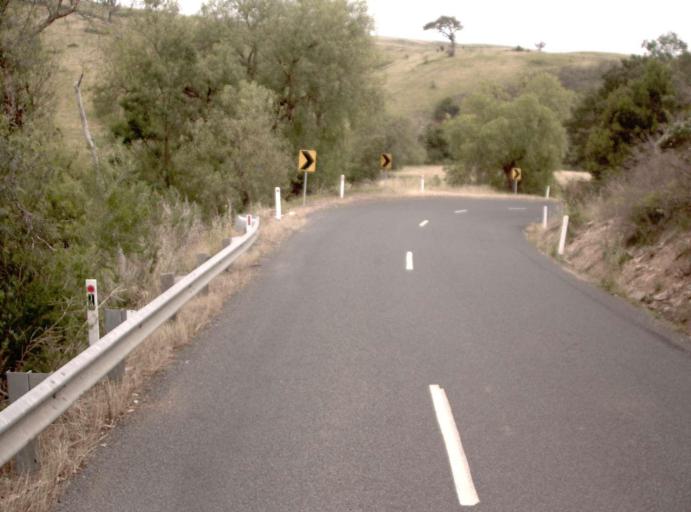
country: AU
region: Victoria
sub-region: Wellington
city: Heyfield
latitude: -37.8557
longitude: 146.7065
